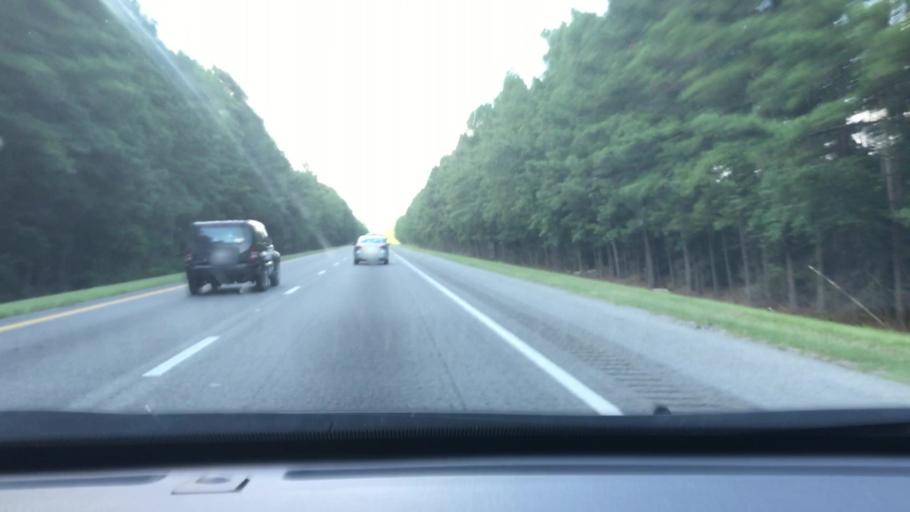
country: US
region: South Carolina
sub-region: Sumter County
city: East Sumter
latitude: 33.9186
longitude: -80.0802
